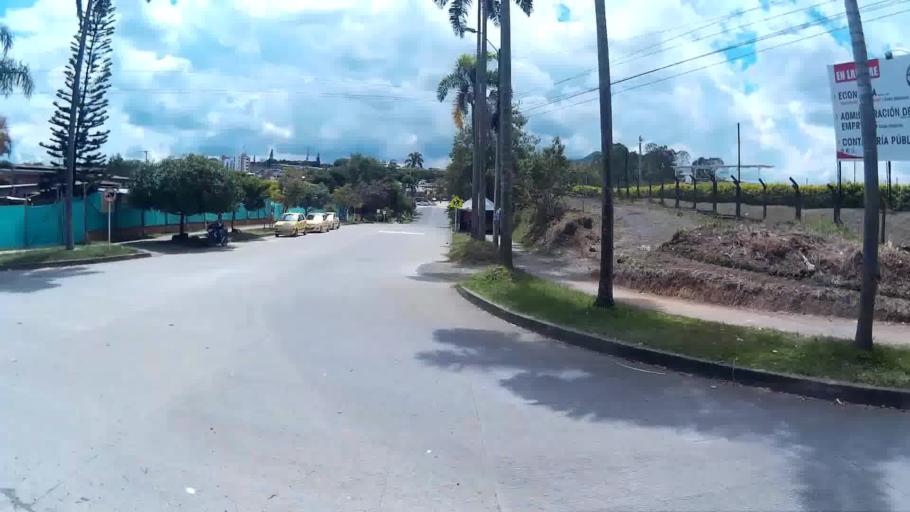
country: CO
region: Risaralda
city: Pereira
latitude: 4.8063
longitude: -75.7621
